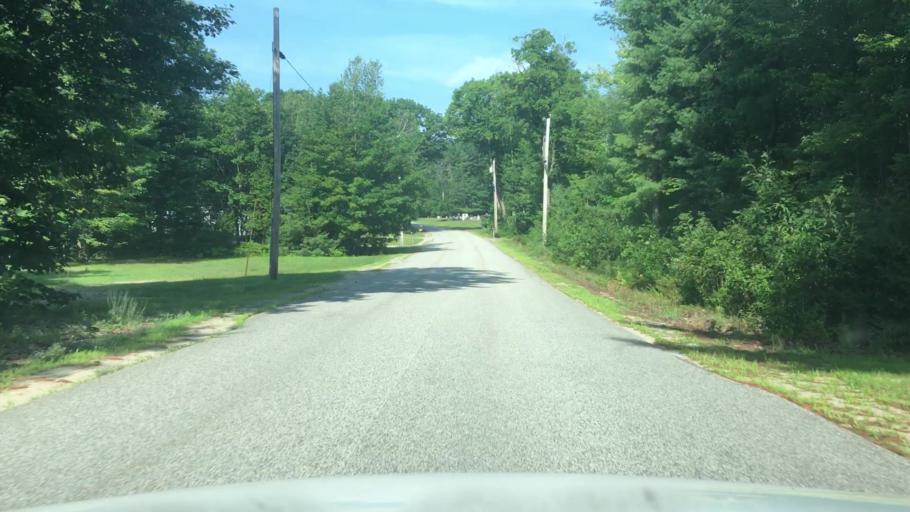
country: US
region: Maine
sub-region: Kennebec County
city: Monmouth
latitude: 44.2431
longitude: -70.0934
